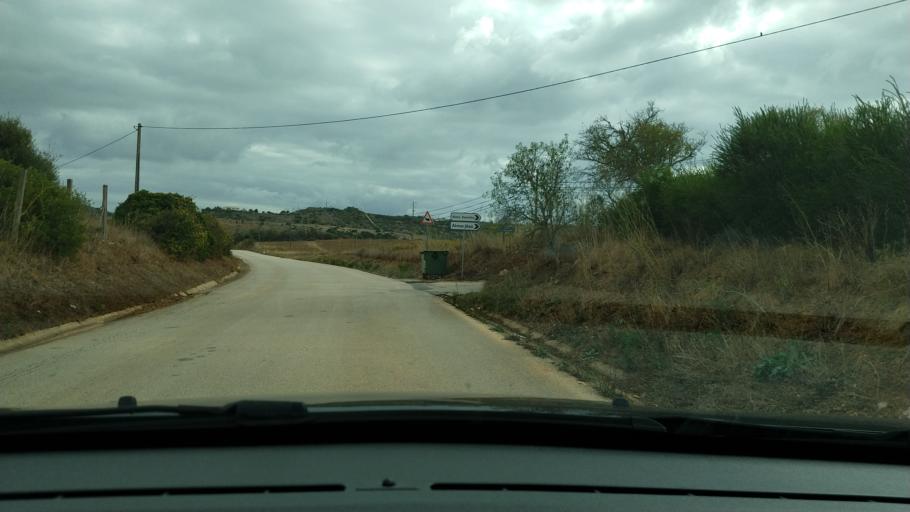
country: PT
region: Faro
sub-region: Lagos
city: Lagos
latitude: 37.0893
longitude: -8.7827
